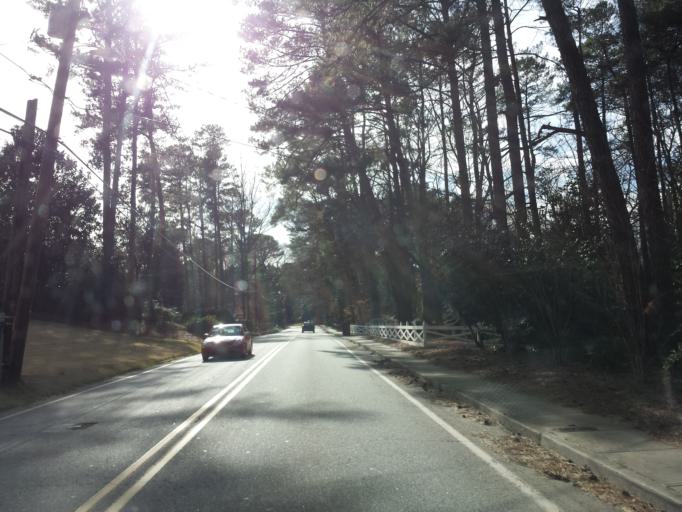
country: US
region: Georgia
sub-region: Cobb County
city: Vinings
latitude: 33.8291
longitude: -84.4355
